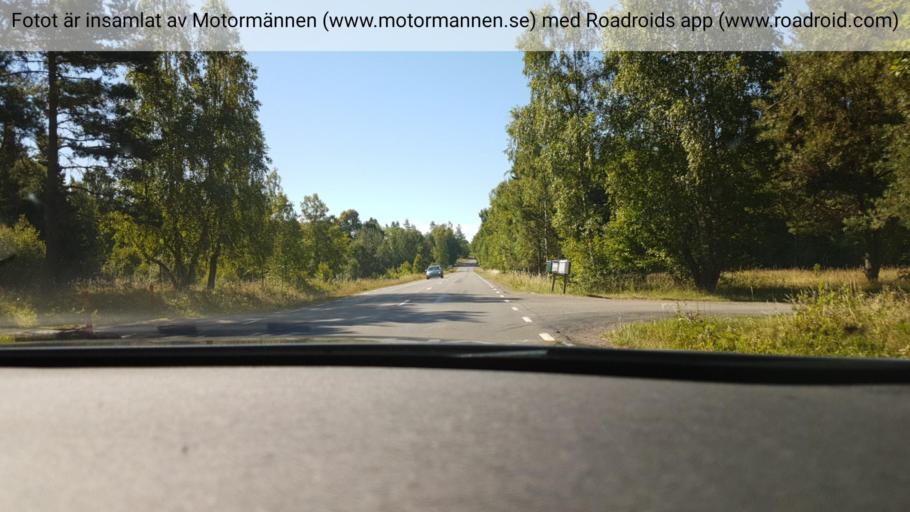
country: SE
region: Vaestra Goetaland
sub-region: Tidaholms Kommun
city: Tidaholm
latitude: 58.1573
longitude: 13.9635
